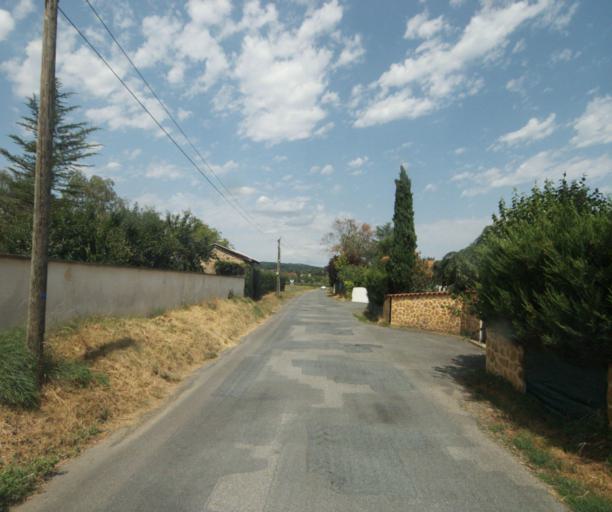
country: FR
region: Rhone-Alpes
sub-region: Departement du Rhone
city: Saint-Germain-Nuelles
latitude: 45.8469
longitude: 4.6143
